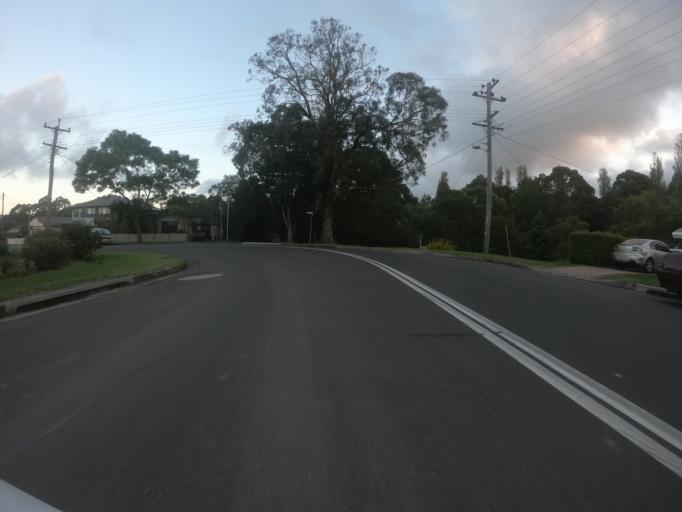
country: AU
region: New South Wales
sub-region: Wollongong
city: Mount Ousley
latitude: -34.3944
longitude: 150.8788
